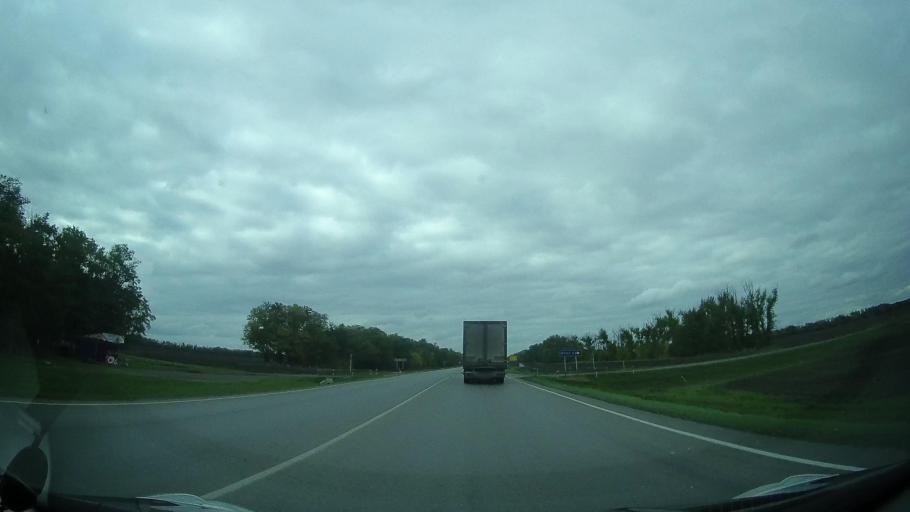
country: RU
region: Rostov
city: Yegorlykskaya
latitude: 46.6236
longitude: 40.5945
